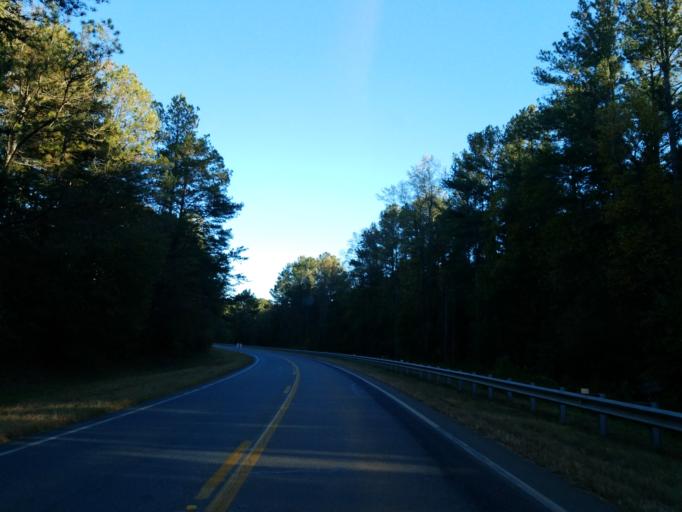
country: US
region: Georgia
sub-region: Dawson County
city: Dawsonville
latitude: 34.4242
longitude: -84.1522
